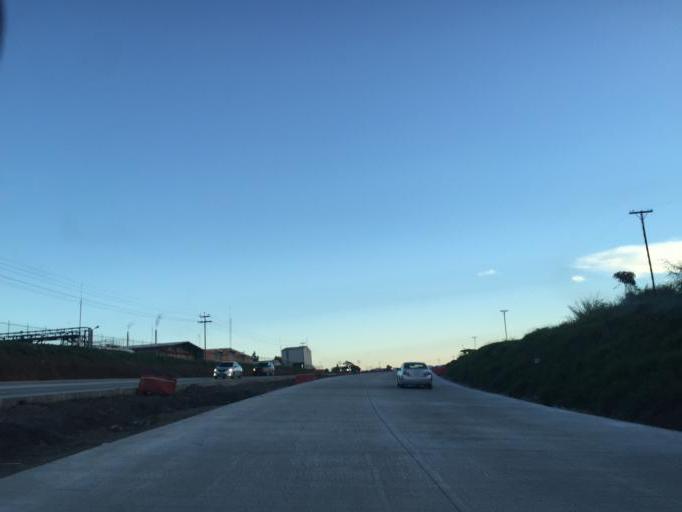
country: MX
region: Veracruz
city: Ixtac Zoquitlan
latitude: 18.8659
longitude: -97.0682
